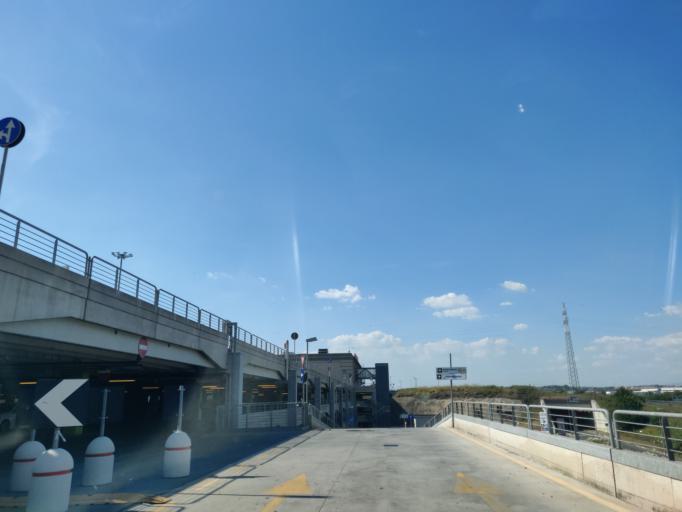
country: IT
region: Latium
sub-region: Citta metropolitana di Roma Capitale
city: Setteville
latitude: 41.9145
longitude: 12.6631
